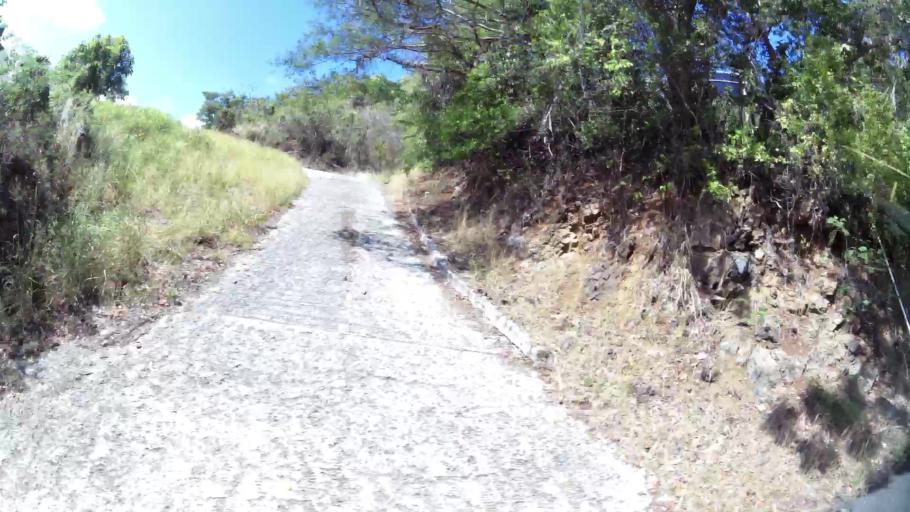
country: VG
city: Tortola
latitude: 18.4296
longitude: -64.6032
